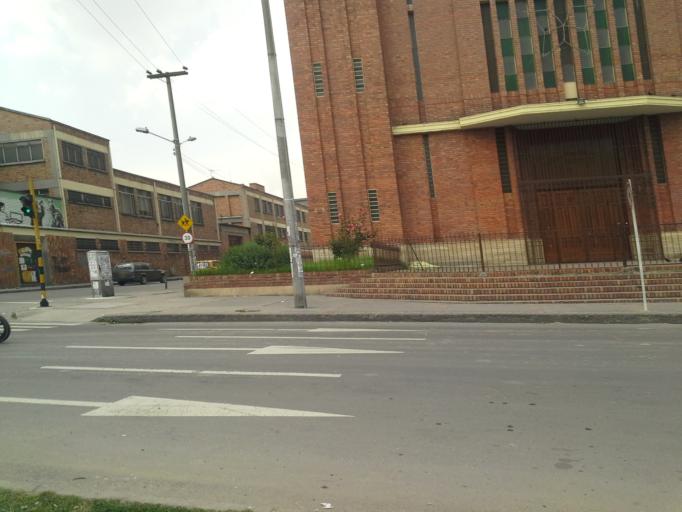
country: CO
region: Bogota D.C.
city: Bogota
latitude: 4.5822
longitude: -74.1084
